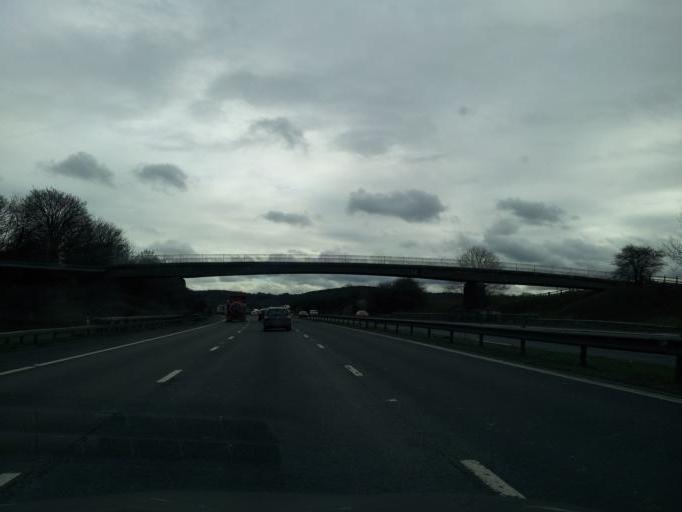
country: GB
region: England
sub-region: Staffordshire
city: Audley
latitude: 53.0307
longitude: -2.3271
